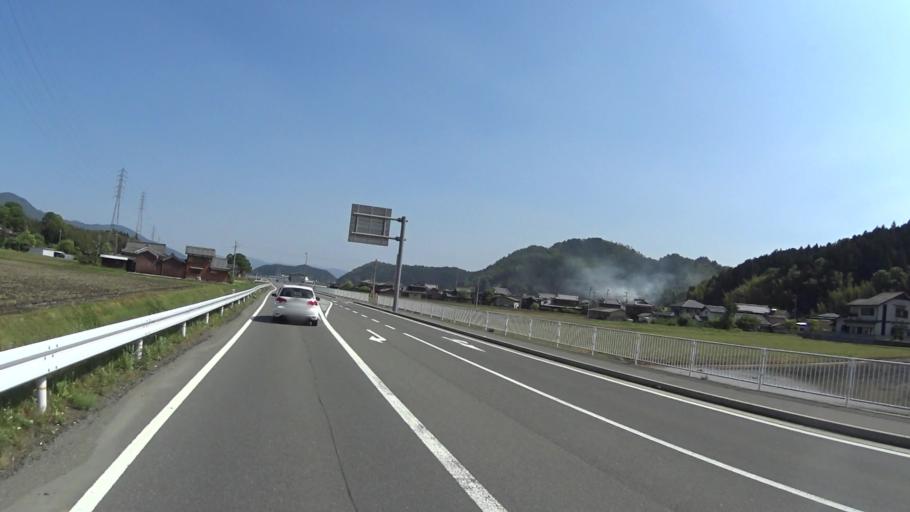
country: JP
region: Kyoto
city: Kameoka
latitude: 35.1041
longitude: 135.5270
